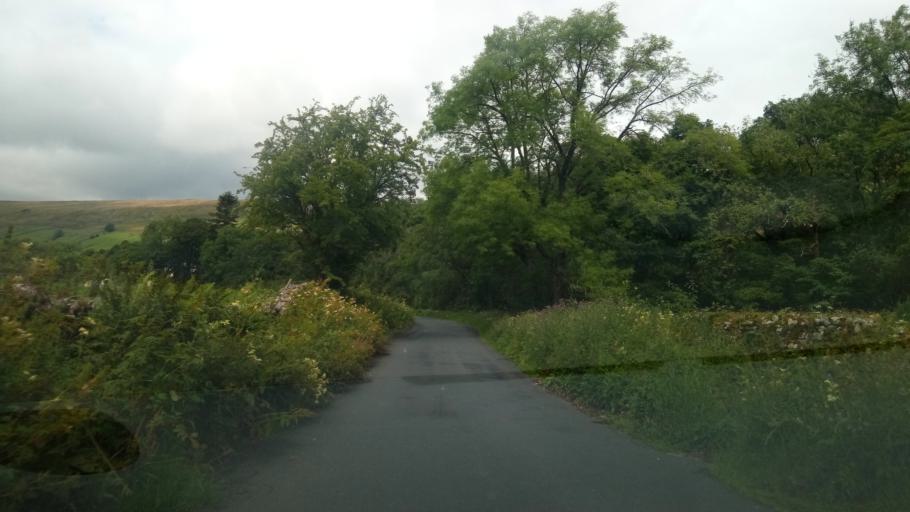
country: GB
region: England
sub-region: North Yorkshire
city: Ingleton
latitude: 54.2758
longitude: -2.3651
